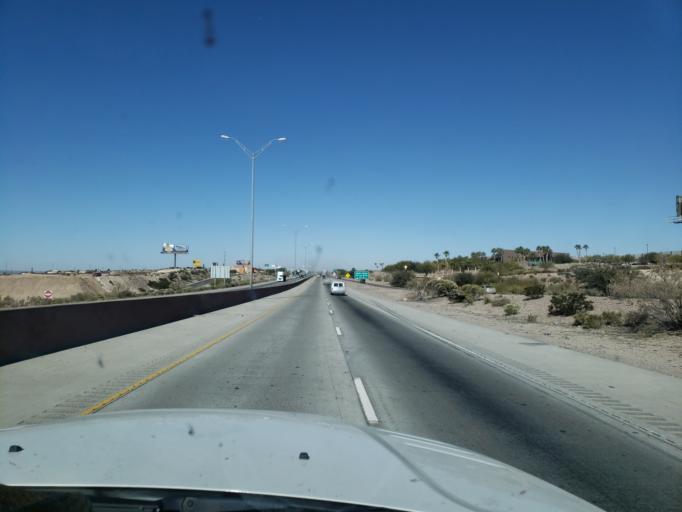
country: US
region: Texas
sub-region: El Paso County
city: Canutillo
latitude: 31.8695
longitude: -106.5785
